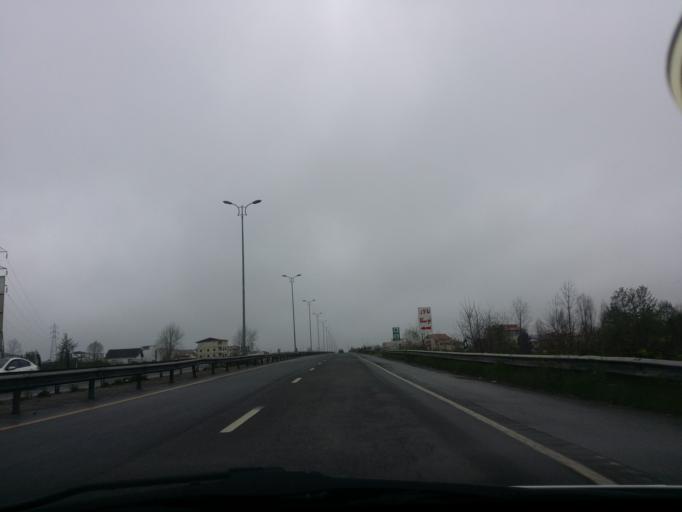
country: IR
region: Mazandaran
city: Tonekabon
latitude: 36.8046
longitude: 50.8766
